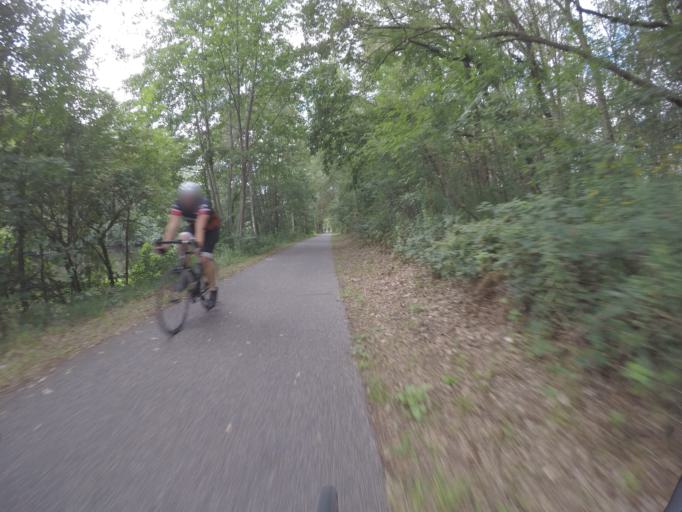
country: DE
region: Brandenburg
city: Hennigsdorf
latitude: 52.6130
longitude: 13.1839
